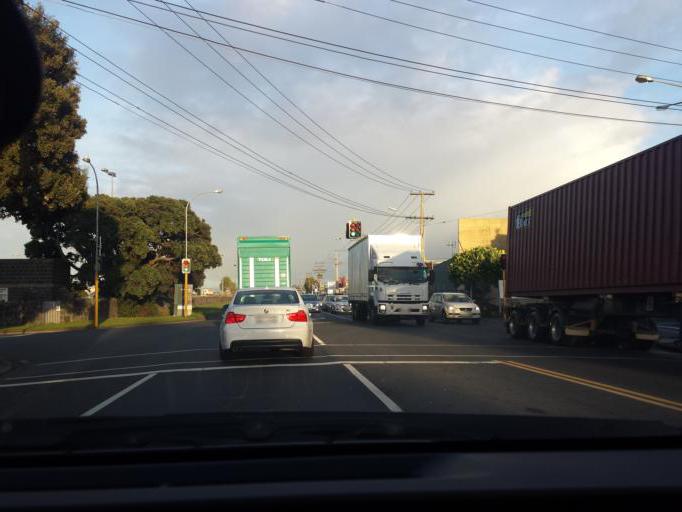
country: NZ
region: Auckland
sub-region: Auckland
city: Mangere
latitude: -36.9260
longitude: 174.8014
